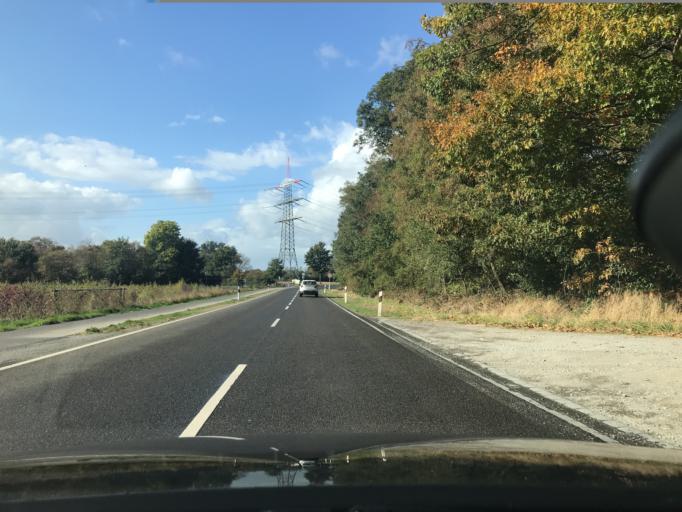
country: DE
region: North Rhine-Westphalia
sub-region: Regierungsbezirk Dusseldorf
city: Meerbusch
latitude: 51.2942
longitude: 6.6414
